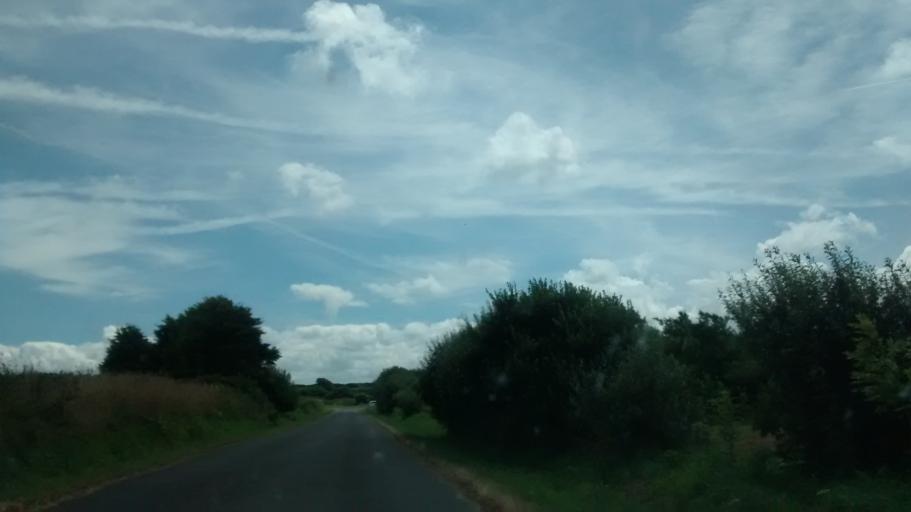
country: FR
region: Brittany
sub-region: Departement du Finistere
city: Plouguerneau
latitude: 48.6207
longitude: -4.4702
